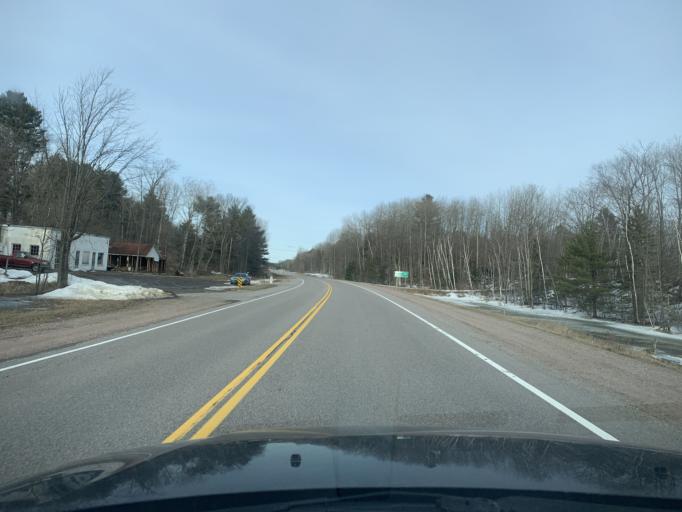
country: CA
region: Ontario
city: Skatepark
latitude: 44.7227
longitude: -76.9722
